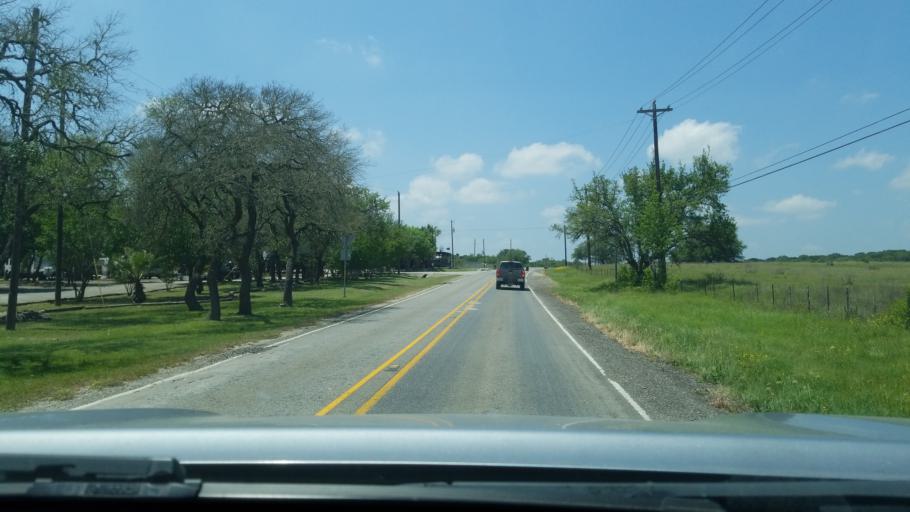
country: US
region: Texas
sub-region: Hays County
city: Woodcreek
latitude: 30.0362
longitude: -98.1820
